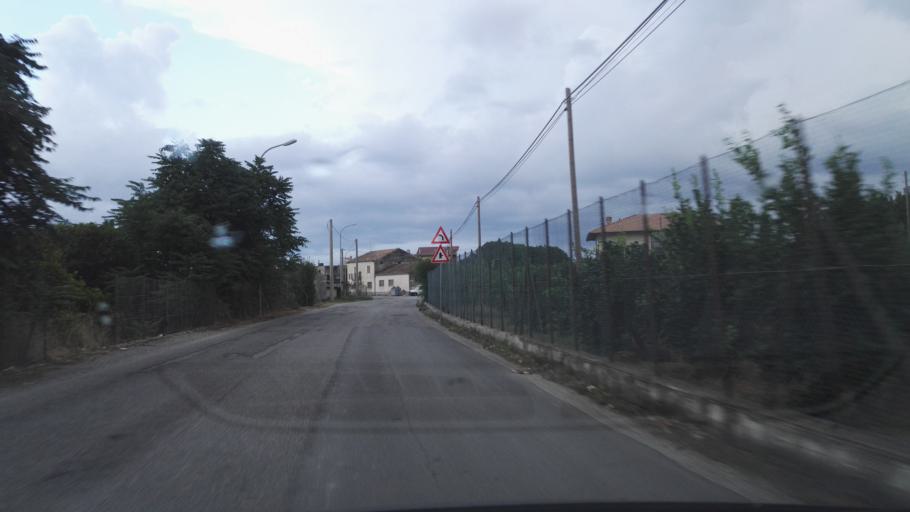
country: IT
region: Calabria
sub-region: Provincia di Reggio Calabria
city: Caulonia Marina
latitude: 38.3560
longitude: 16.4700
